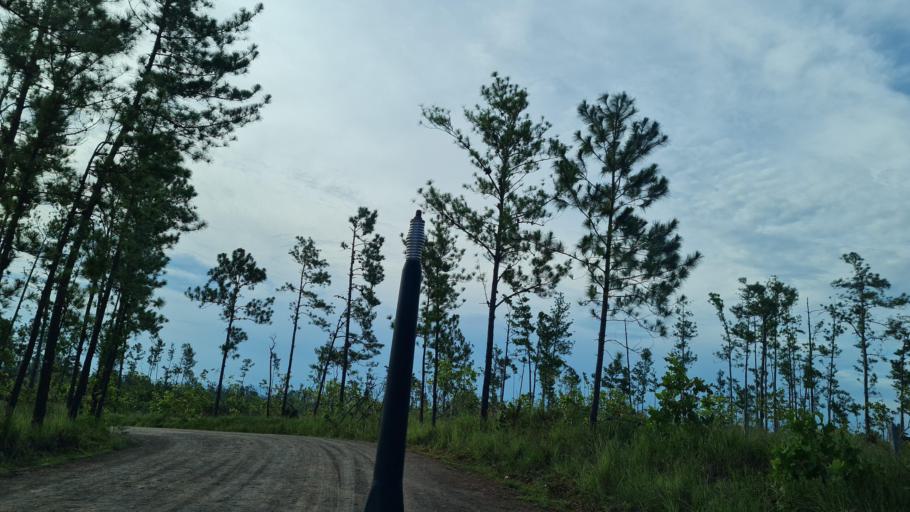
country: NI
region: Atlantico Sur
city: La Cruz de Rio Grande
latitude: 13.5617
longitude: -84.3043
